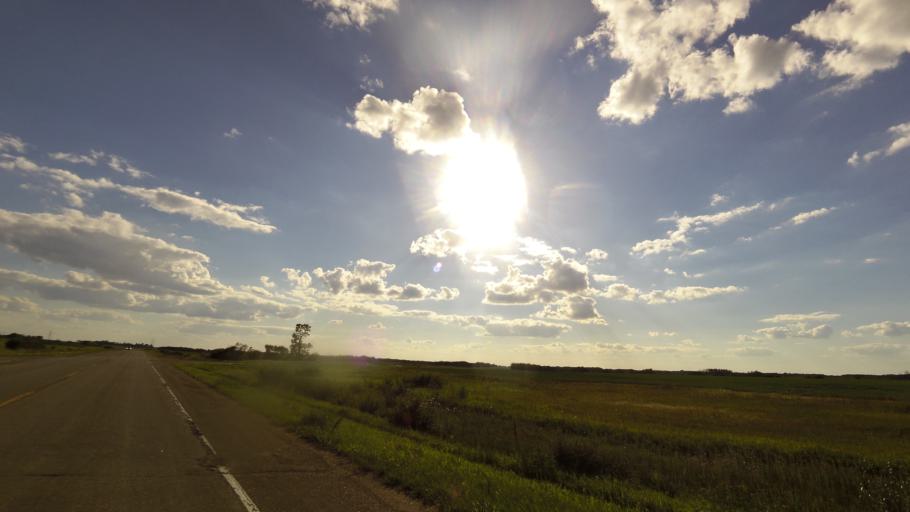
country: CA
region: Saskatchewan
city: Lanigan
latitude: 51.8676
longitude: -105.2061
